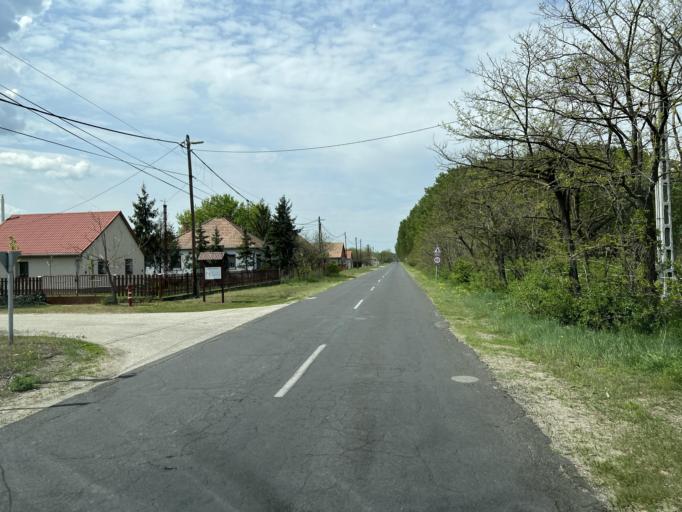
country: HU
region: Pest
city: Csemo
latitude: 47.1223
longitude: 19.6893
